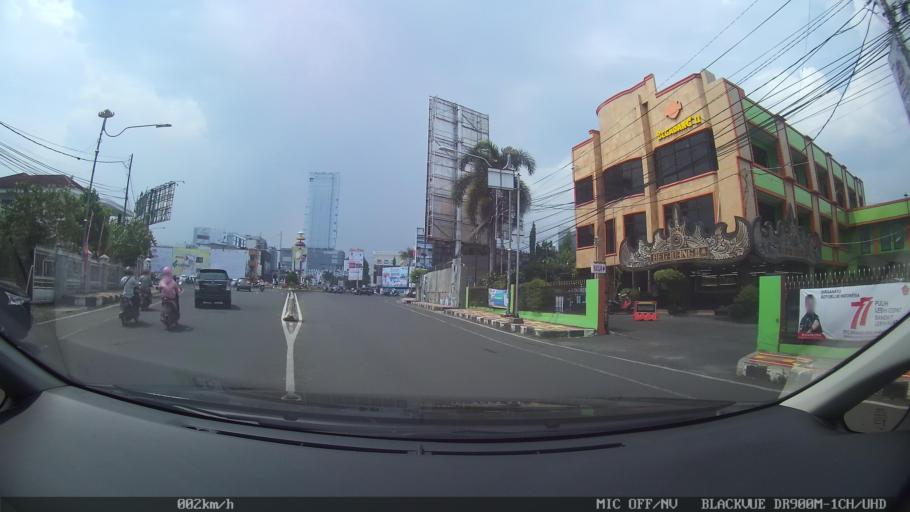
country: ID
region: Lampung
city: Bandarlampung
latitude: -5.4232
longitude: 105.2583
